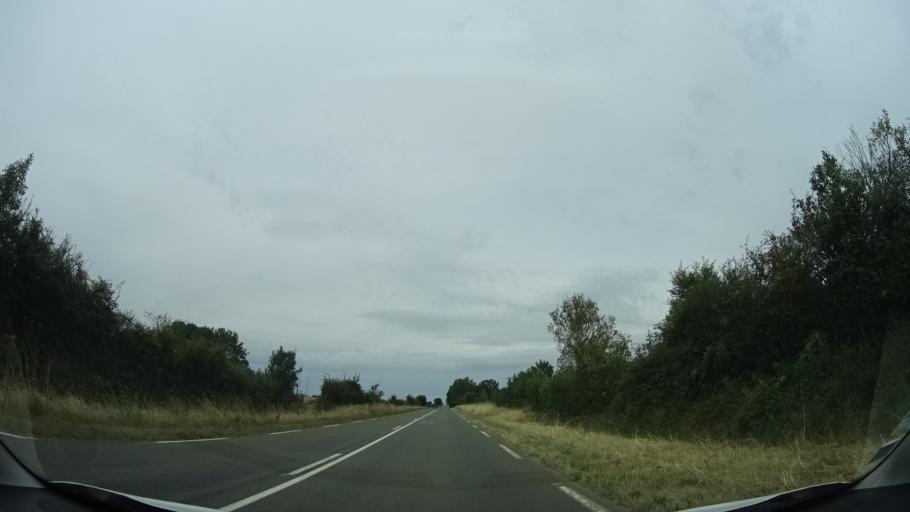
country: FR
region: Pays de la Loire
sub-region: Departement de la Mayenne
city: Meslay-du-Maine
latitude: 47.9321
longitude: -0.4987
